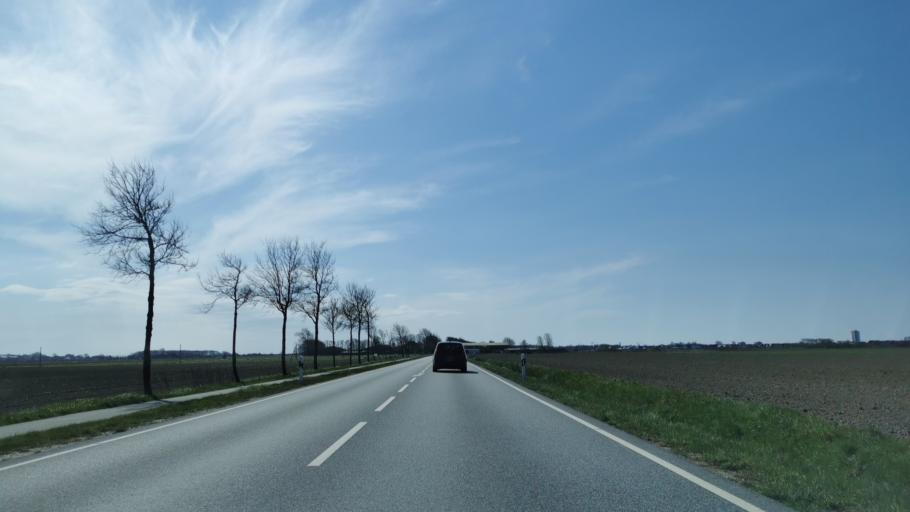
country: DE
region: Schleswig-Holstein
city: Oesterdeichstrich
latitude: 54.1538
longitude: 8.8792
